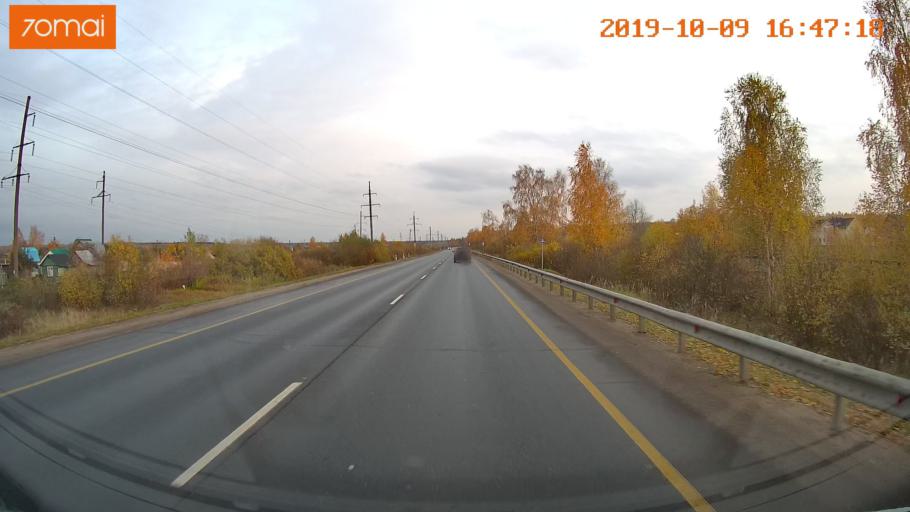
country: RU
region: Kostroma
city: Volgorechensk
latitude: 57.4378
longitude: 41.1760
